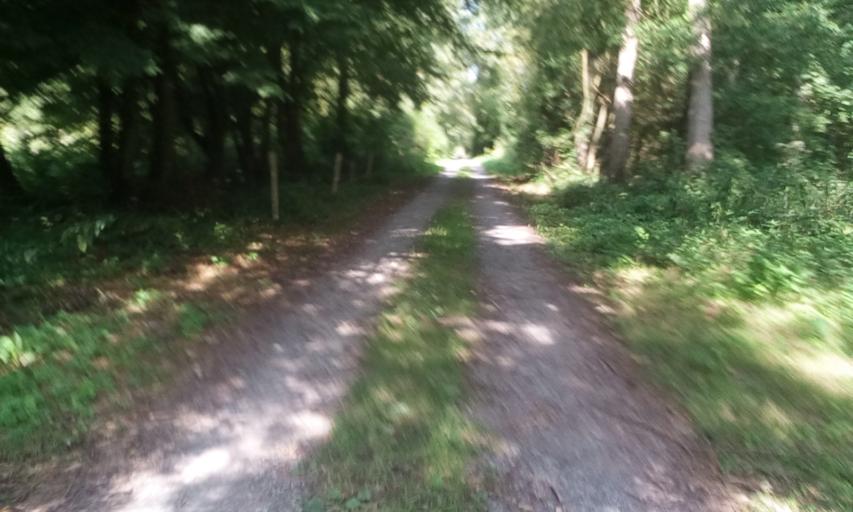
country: FR
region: Lower Normandy
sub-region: Departement du Calvados
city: Argences
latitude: 49.1395
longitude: -0.1709
